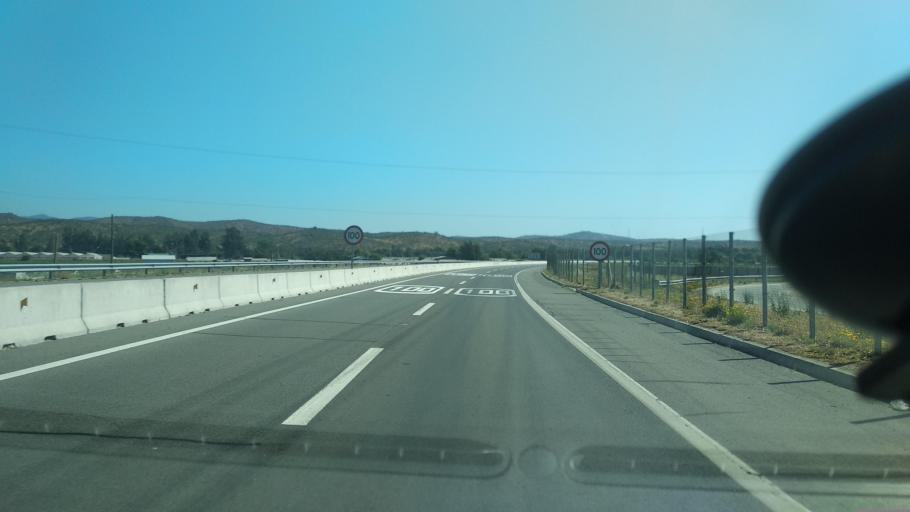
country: CL
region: Valparaiso
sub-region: Provincia de Marga Marga
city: Limache
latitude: -32.9770
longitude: -71.3049
